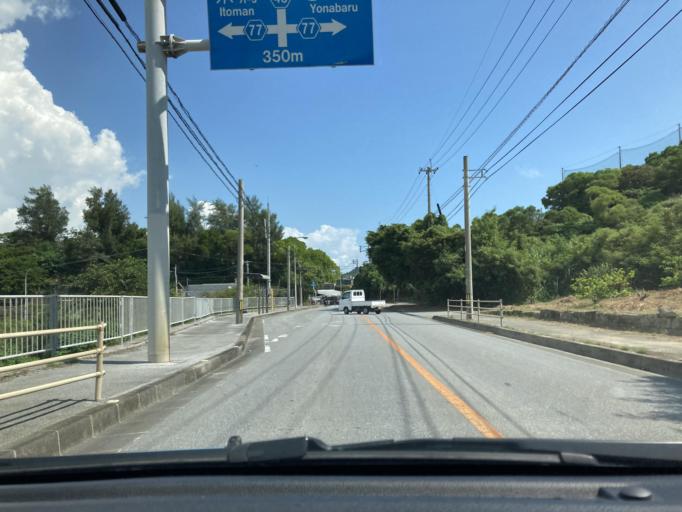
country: JP
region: Okinawa
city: Tomigusuku
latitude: 26.1666
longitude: 127.7399
